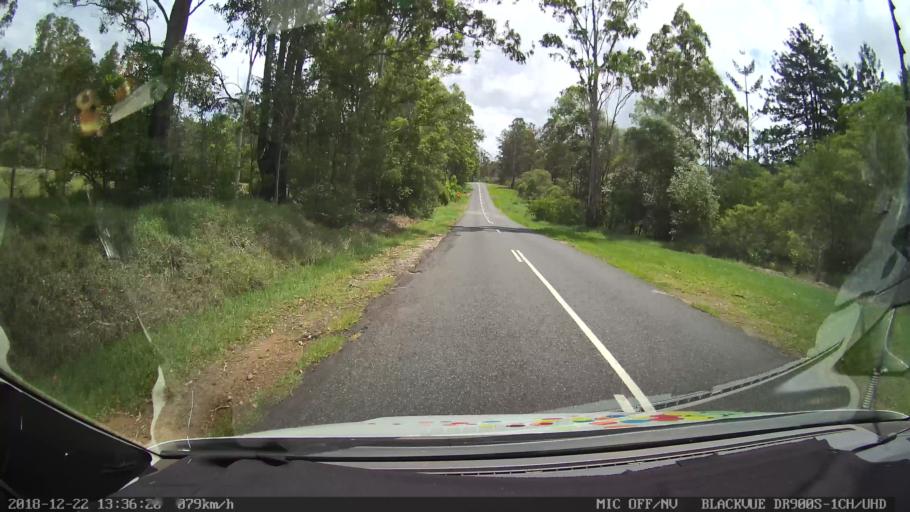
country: AU
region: New South Wales
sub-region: Clarence Valley
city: Coutts Crossing
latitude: -29.8794
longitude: 152.7960
